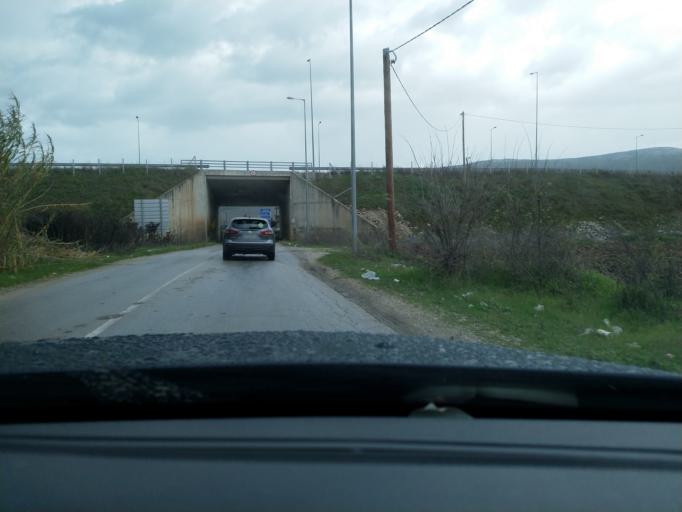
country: GR
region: Thessaly
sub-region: Trikala
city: Taxiarches
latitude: 39.5620
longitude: 21.8893
